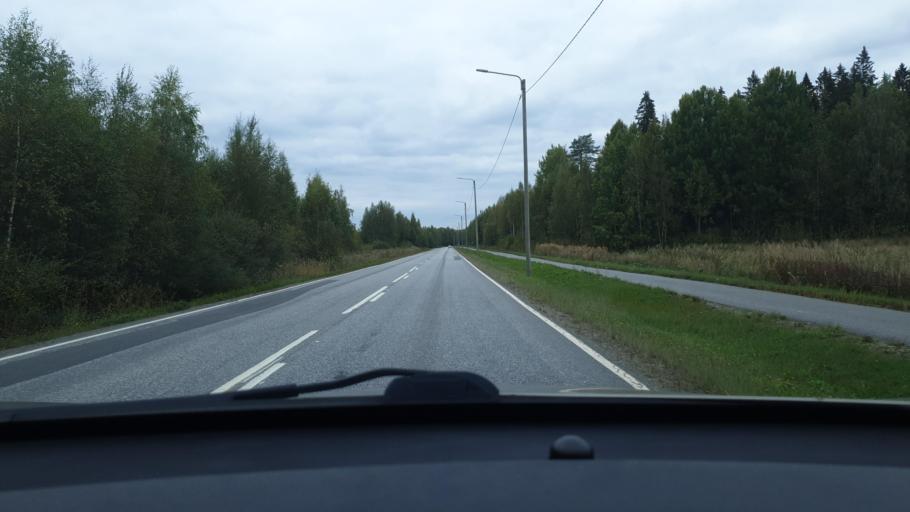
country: FI
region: Ostrobothnia
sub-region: Vaasa
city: Ristinummi
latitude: 63.0603
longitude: 21.7110
